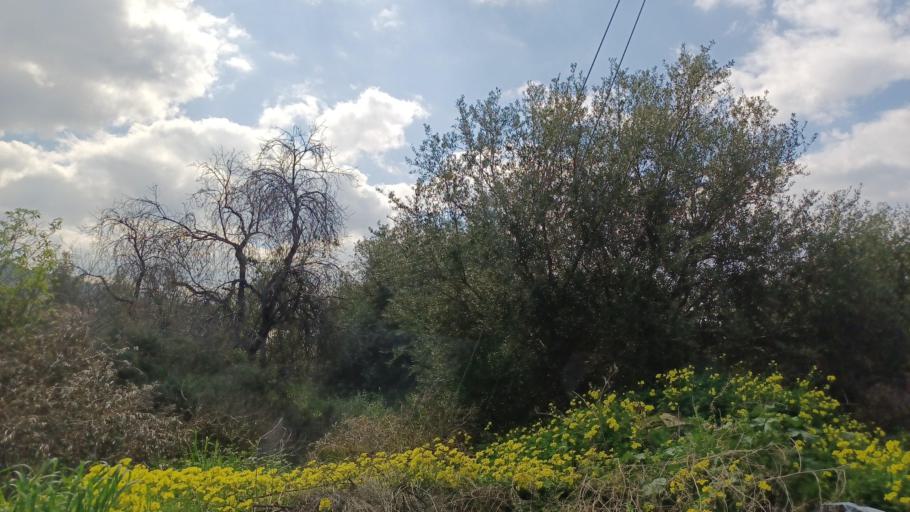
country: CY
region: Pafos
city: Polis
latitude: 35.1129
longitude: 32.5155
